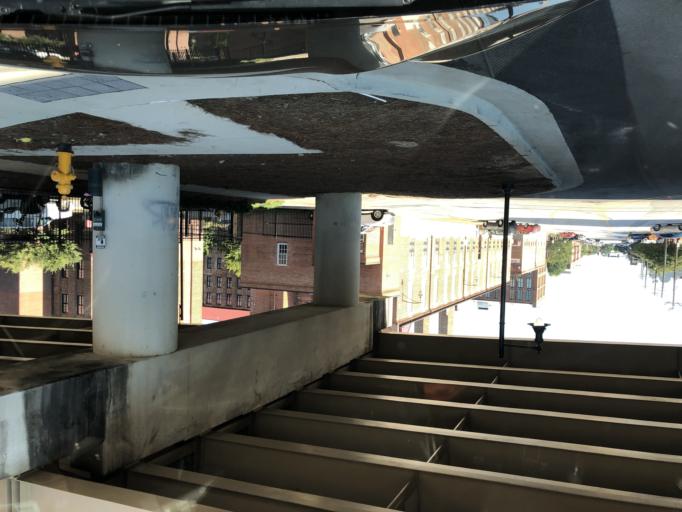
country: US
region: Alabama
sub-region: Russell County
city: Phenix City
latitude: 32.4707
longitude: -84.9946
